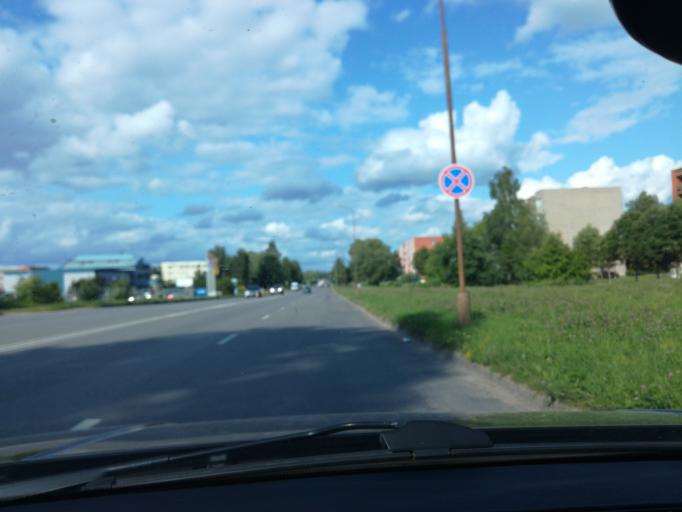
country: LT
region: Alytaus apskritis
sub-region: Alytus
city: Alytus
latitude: 54.4102
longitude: 24.0071
